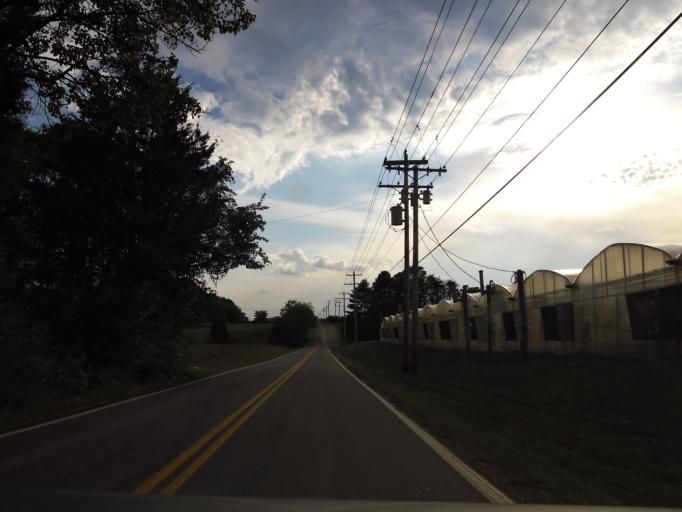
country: US
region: Tennessee
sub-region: Blount County
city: Alcoa
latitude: 35.8062
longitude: -83.9557
